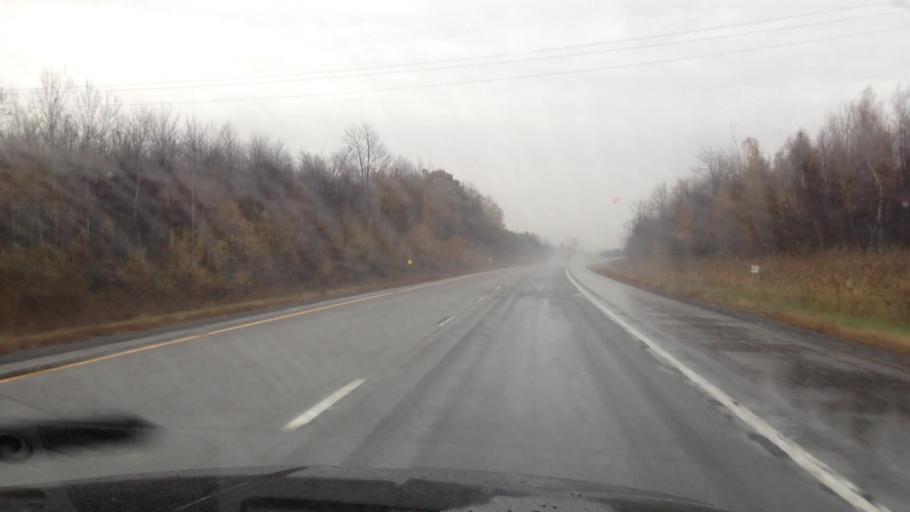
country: CA
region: Ontario
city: Casselman
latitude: 45.3047
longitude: -75.1137
